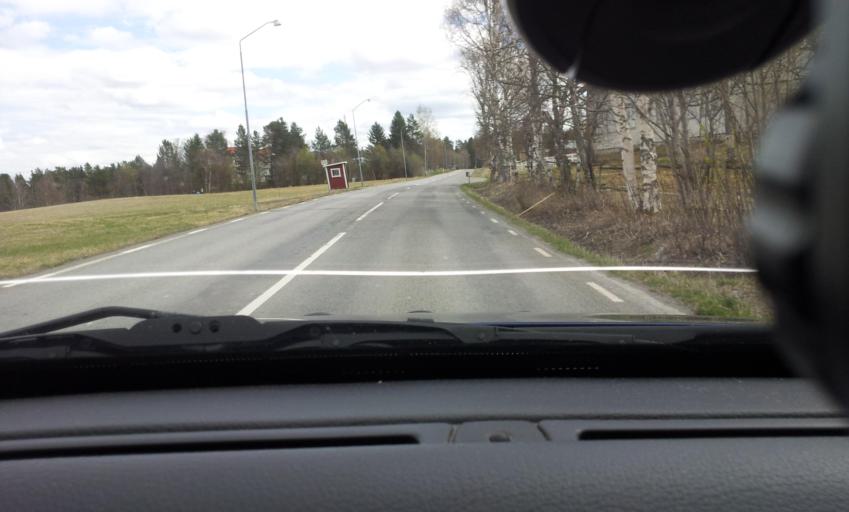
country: SE
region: Jaemtland
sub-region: OEstersunds Kommun
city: Ostersund
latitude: 63.1506
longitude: 14.5965
